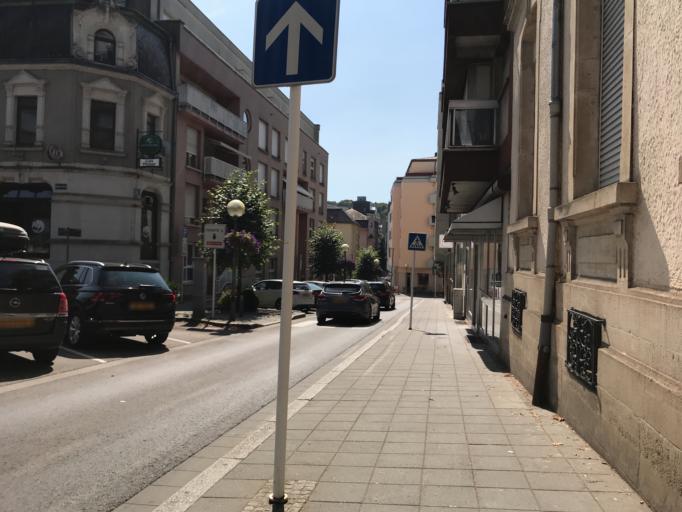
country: LU
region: Luxembourg
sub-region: Canton d'Esch-sur-Alzette
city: Esch-sur-Alzette
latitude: 49.4966
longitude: 5.9812
